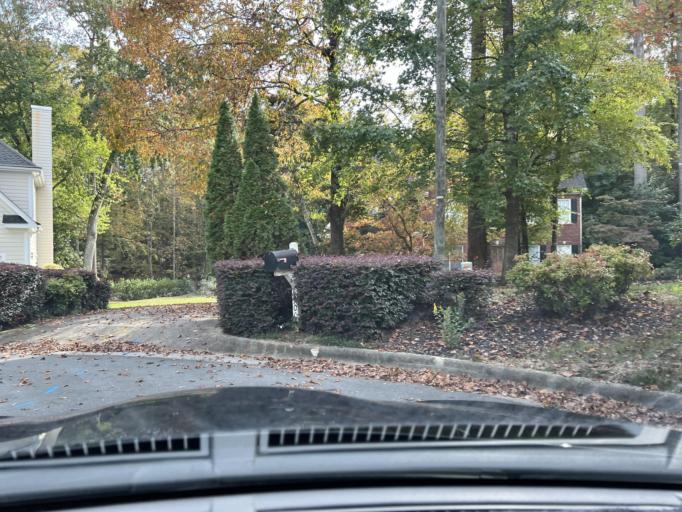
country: US
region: North Carolina
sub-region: Wake County
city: Wake Forest
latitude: 35.8951
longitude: -78.5835
